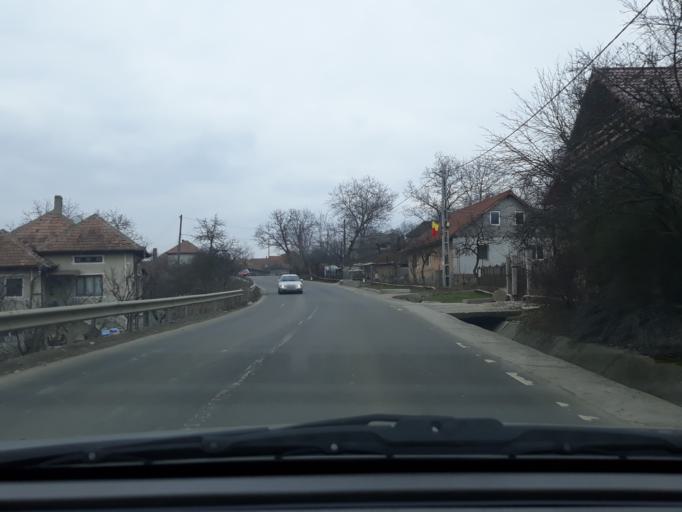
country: RO
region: Salaj
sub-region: Comuna Criseni
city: Criseni
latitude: 47.2363
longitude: 23.0542
